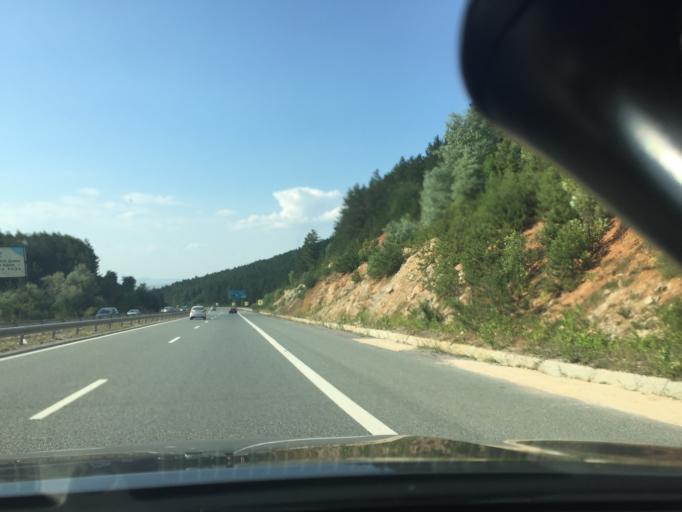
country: BG
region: Pernik
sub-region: Obshtina Pernik
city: Pernik
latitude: 42.5157
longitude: 23.1405
